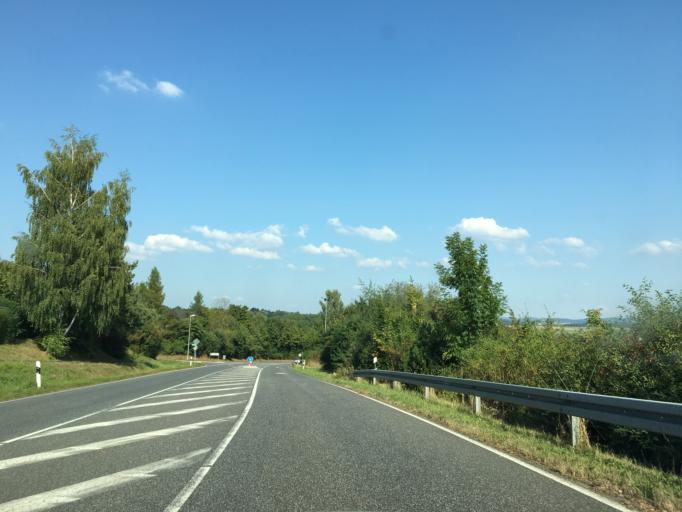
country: DE
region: Hesse
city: Frankenberg
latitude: 51.0486
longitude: 8.7973
